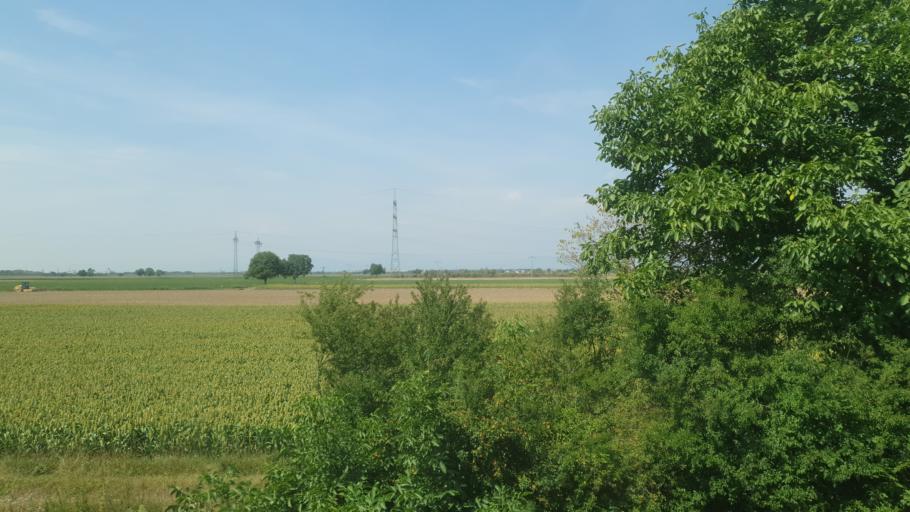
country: DE
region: Baden-Wuerttemberg
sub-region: Freiburg Region
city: Auggen
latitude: 47.7981
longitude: 7.5921
